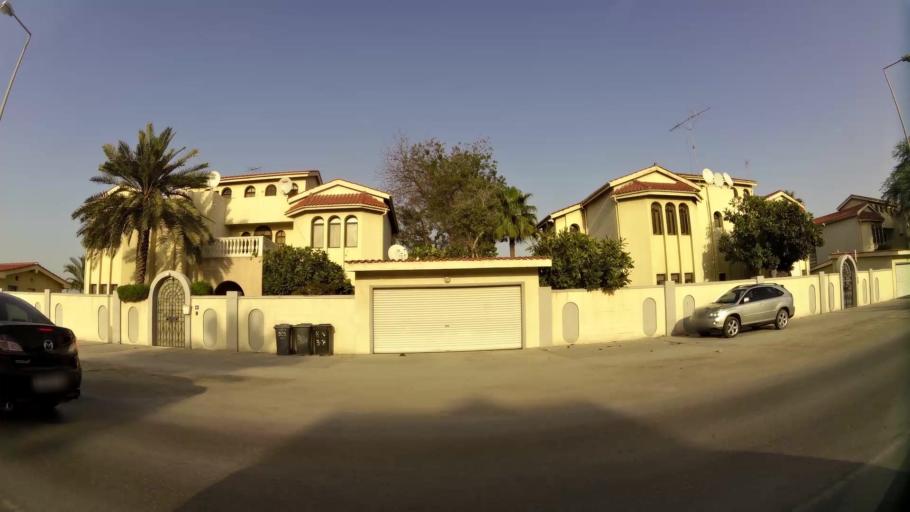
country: BH
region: Manama
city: Jidd Hafs
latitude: 26.2002
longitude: 50.4848
